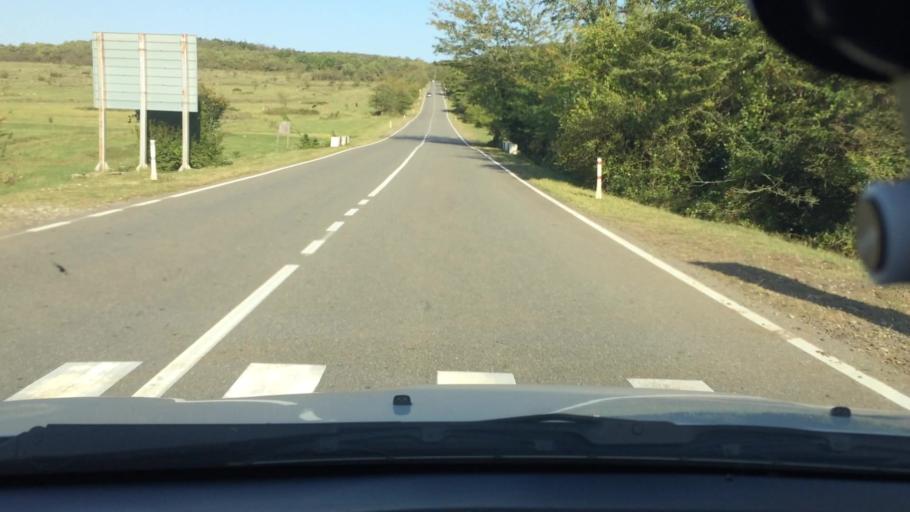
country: GE
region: Imereti
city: Kutaisi
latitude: 42.2411
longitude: 42.7645
